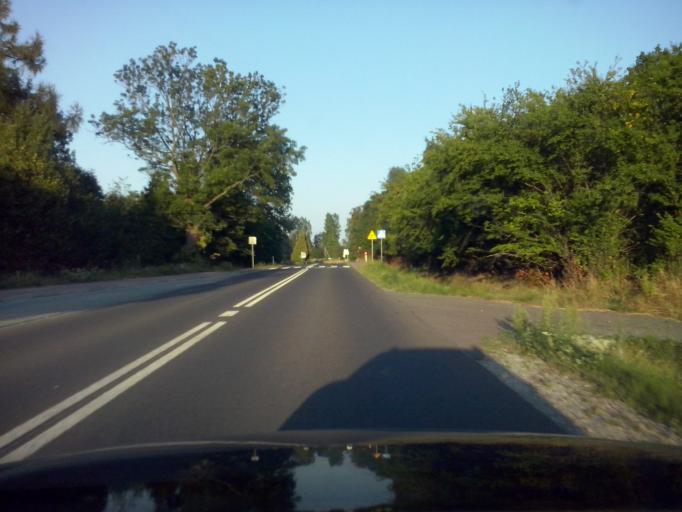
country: PL
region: Swietokrzyskie
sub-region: Powiat buski
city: Gnojno
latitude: 50.6061
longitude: 20.8314
